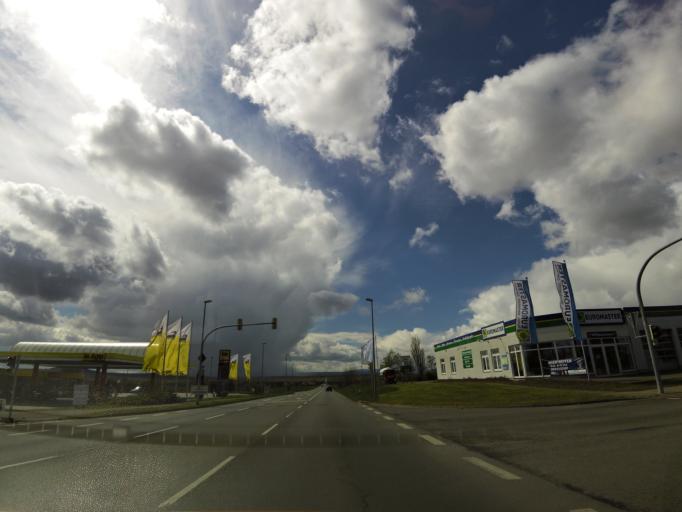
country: DE
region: Saxony-Anhalt
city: Halberstadt
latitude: 51.8857
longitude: 11.0307
